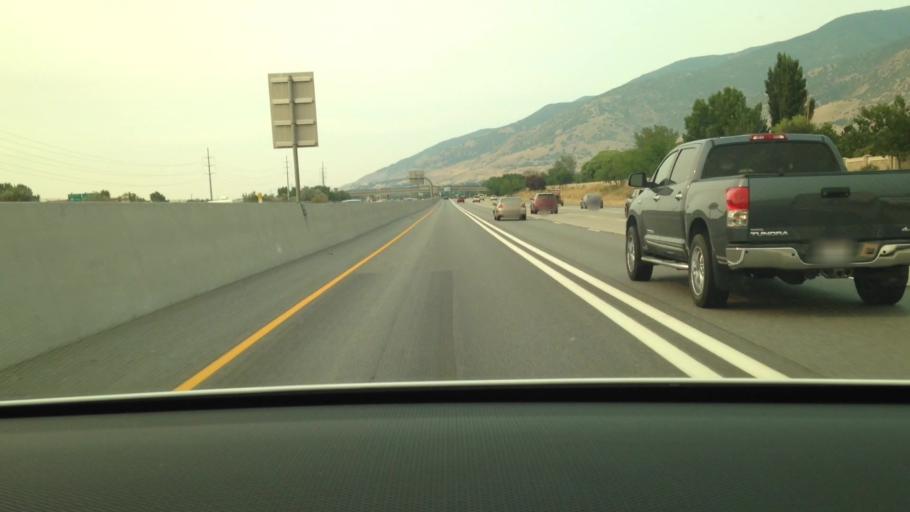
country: US
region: Utah
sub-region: Davis County
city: Farmington
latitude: 40.9582
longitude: -111.8912
